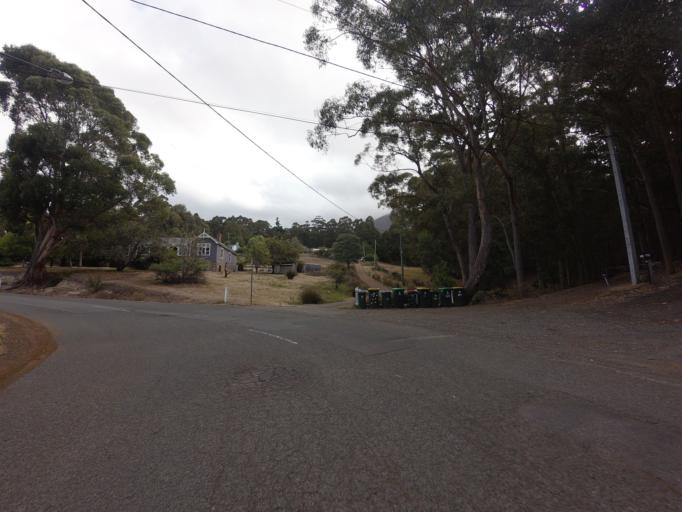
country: AU
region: Tasmania
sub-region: Hobart
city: Dynnyrne
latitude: -42.9013
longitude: 147.2703
